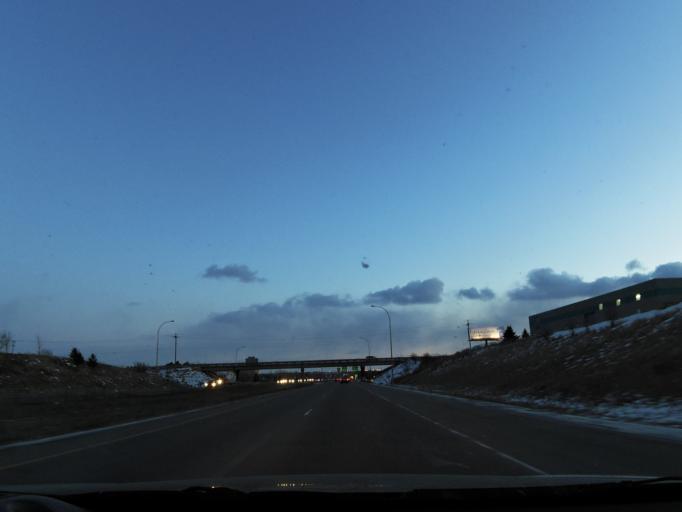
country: US
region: Minnesota
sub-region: Washington County
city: Oakdale
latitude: 44.9548
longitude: -92.9588
